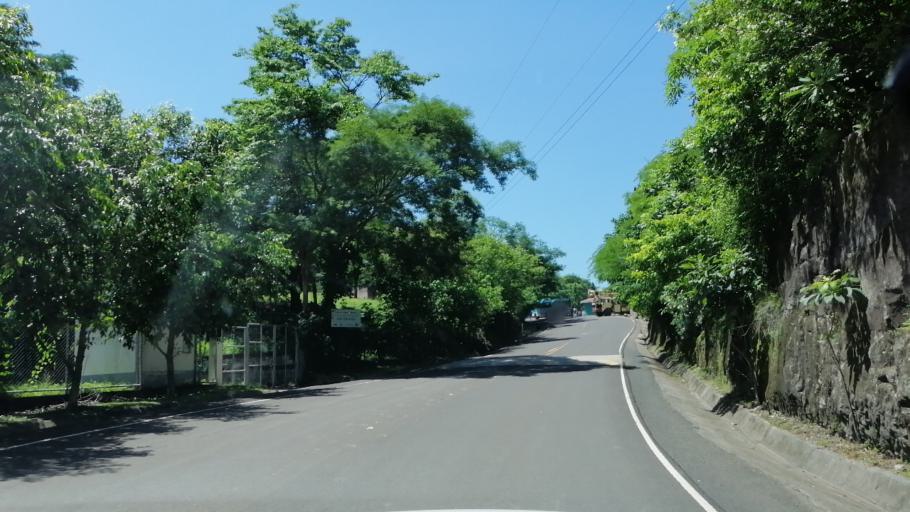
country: SV
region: San Miguel
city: Sesori
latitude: 13.8059
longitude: -88.3970
